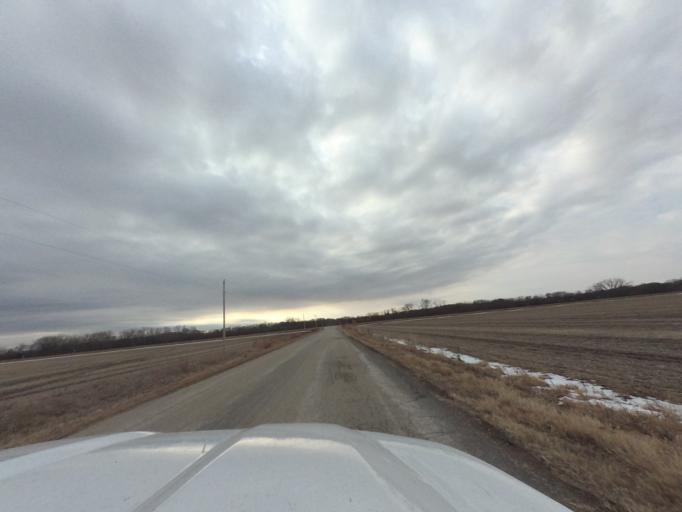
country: US
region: Kansas
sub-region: Chase County
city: Cottonwood Falls
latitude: 38.4091
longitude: -96.3733
